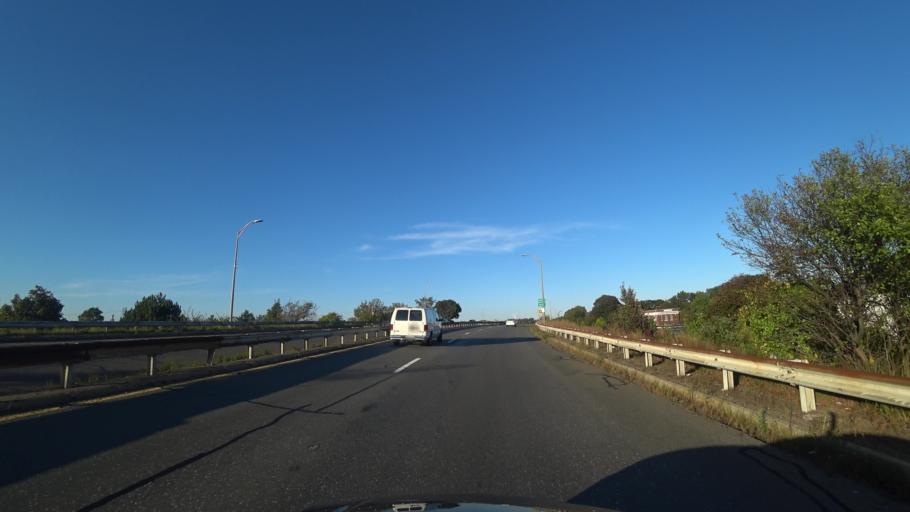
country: US
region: Massachusetts
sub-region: Essex County
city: Lynn
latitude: 42.4391
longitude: -70.9696
